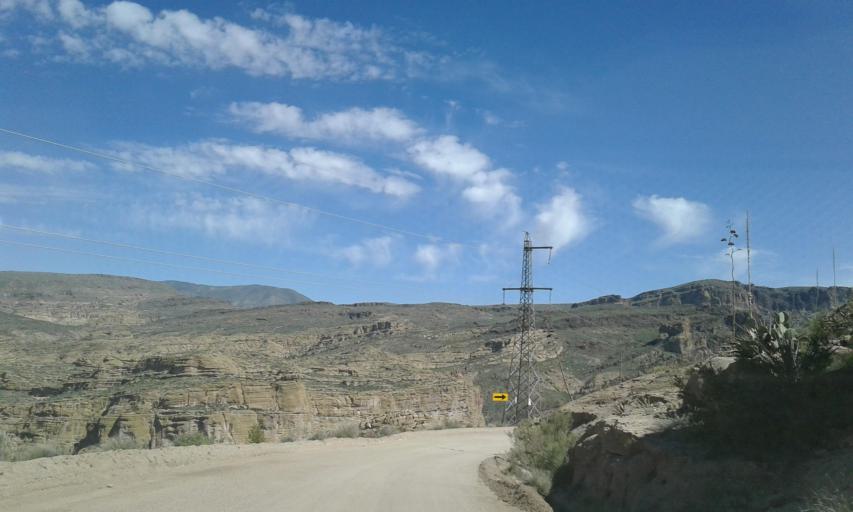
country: US
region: Arizona
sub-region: Pinal County
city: Gold Camp
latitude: 33.5349
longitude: -111.3115
